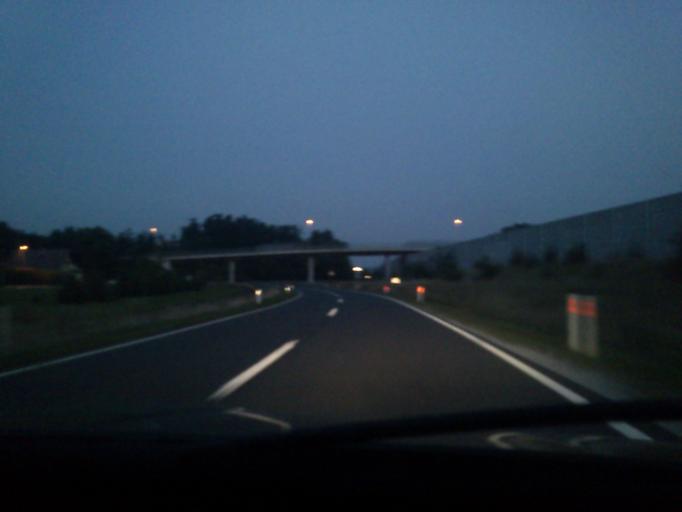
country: SI
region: Hajdina
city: Spodnja Hajdina
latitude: 46.3948
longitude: 15.8530
